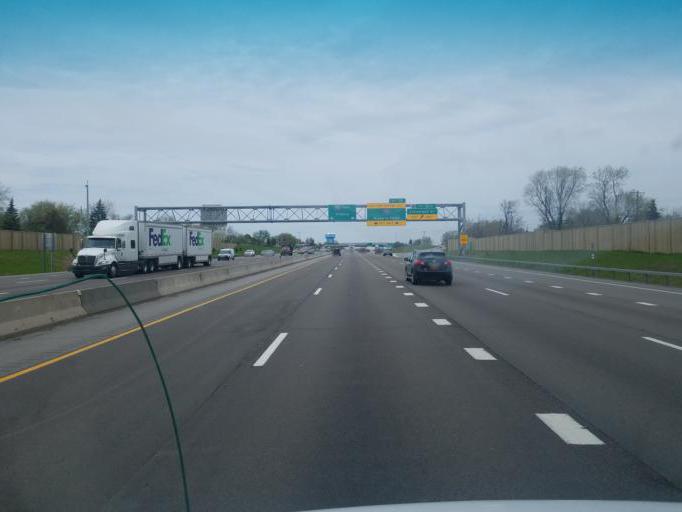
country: US
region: New York
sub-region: Erie County
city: Williamsville
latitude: 42.9402
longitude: -78.7663
